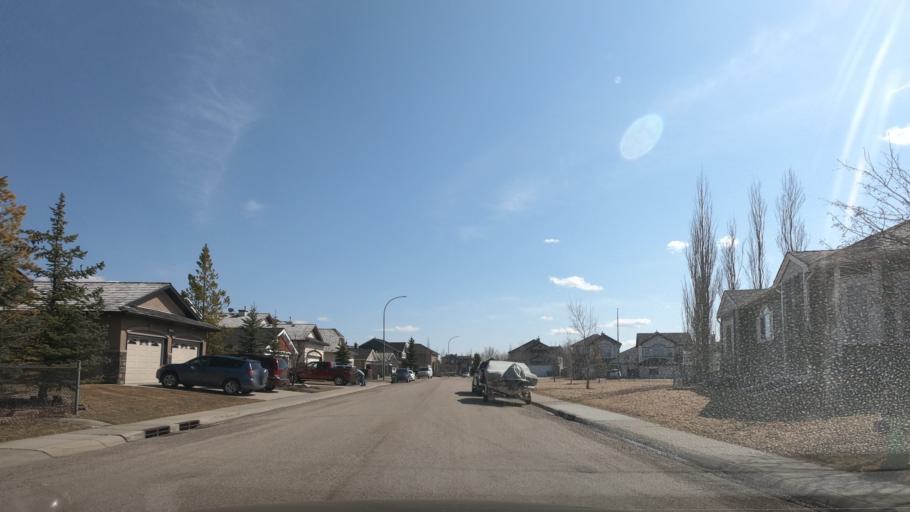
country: CA
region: Alberta
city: Airdrie
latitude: 51.2974
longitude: -114.0466
